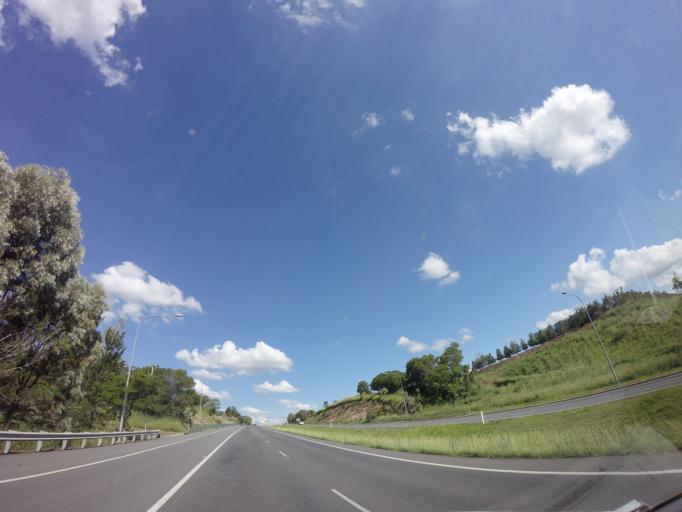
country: AU
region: Queensland
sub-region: Ipswich
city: Thagoona
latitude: -27.5638
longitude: 152.5999
